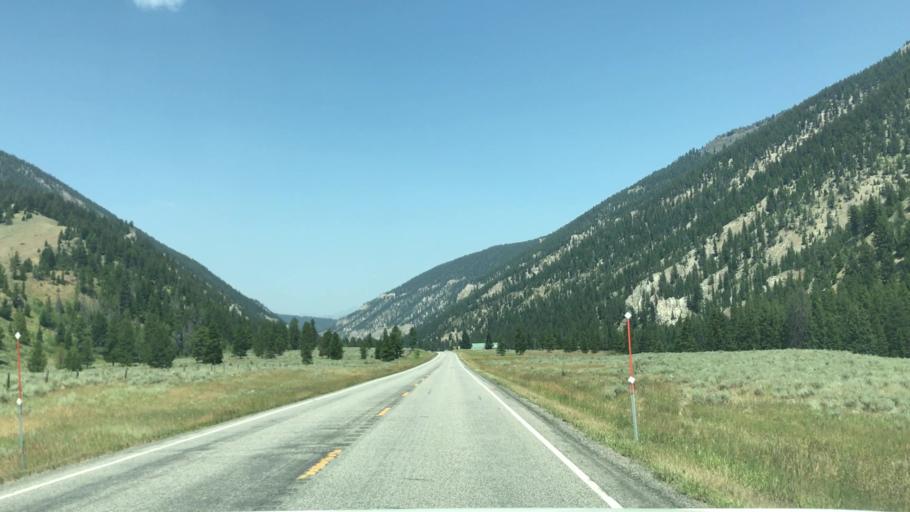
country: US
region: Montana
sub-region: Gallatin County
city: Big Sky
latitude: 45.1097
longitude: -111.2234
